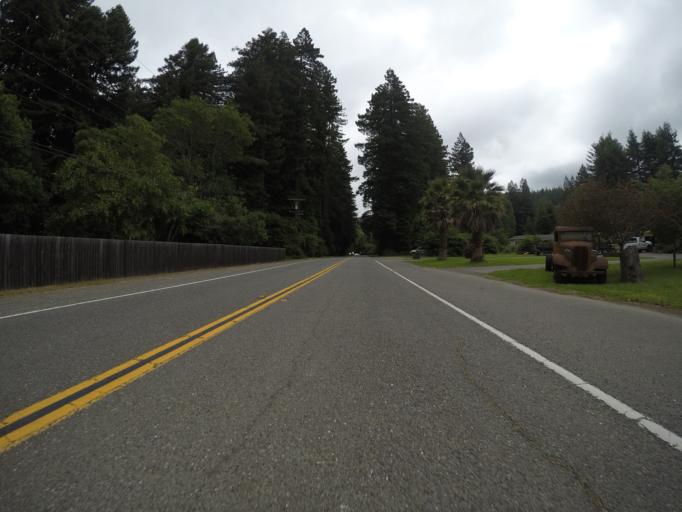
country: US
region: California
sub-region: Humboldt County
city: Rio Dell
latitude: 40.4000
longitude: -123.9489
